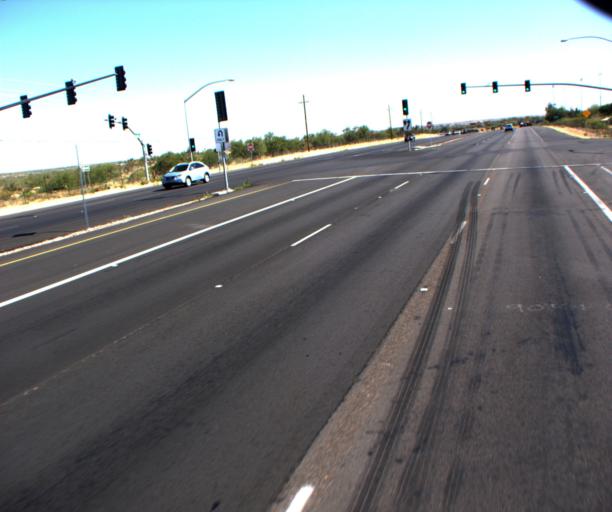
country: US
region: Arizona
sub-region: Pima County
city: Catalina
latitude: 32.4741
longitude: -110.9230
